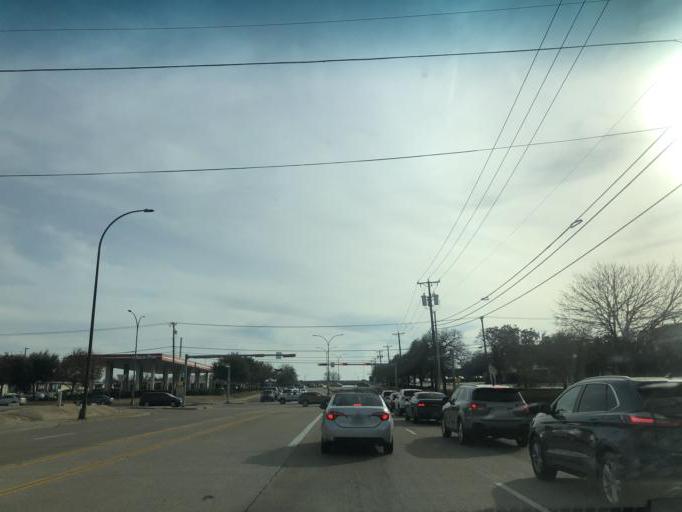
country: US
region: Texas
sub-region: Tarrant County
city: Dalworthington Gardens
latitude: 32.6785
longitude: -97.1496
